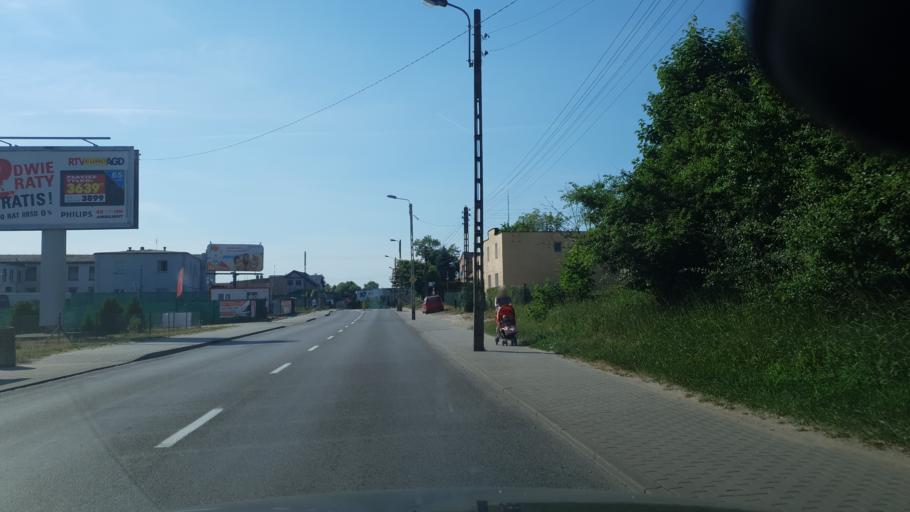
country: PL
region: Pomeranian Voivodeship
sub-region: Gdynia
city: Wielki Kack
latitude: 54.4392
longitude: 18.4594
